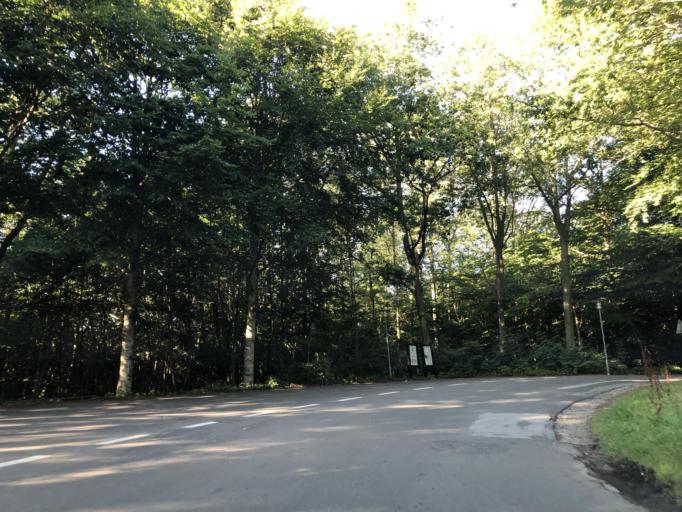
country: DK
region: North Denmark
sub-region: Mariagerfjord Kommune
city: Hobro
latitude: 56.6343
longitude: 9.8295
